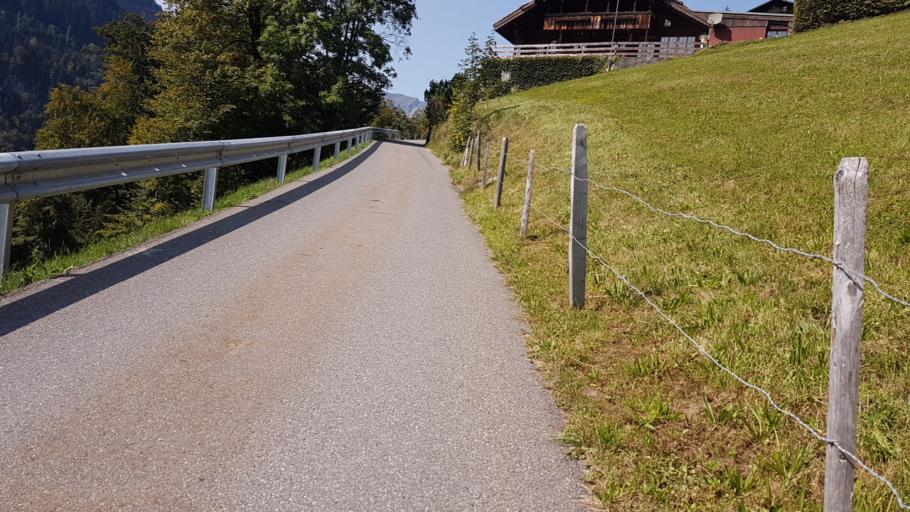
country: CH
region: Bern
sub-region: Frutigen-Niedersimmental District
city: Aeschi
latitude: 46.5937
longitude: 7.7169
